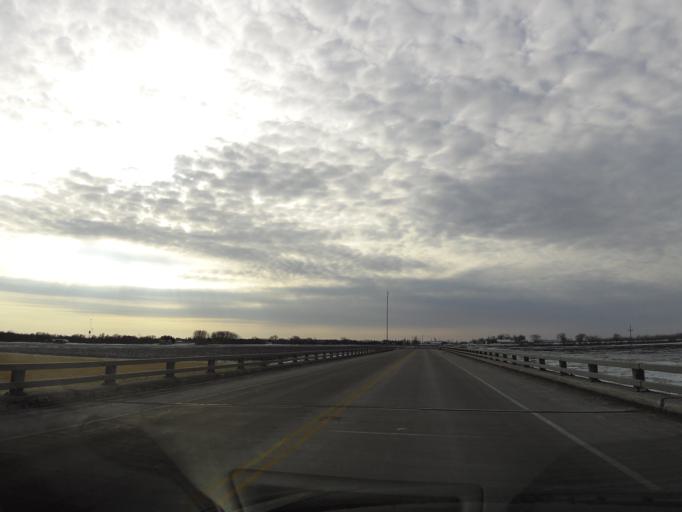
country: US
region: Minnesota
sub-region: Kittson County
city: Hallock
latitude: 48.5717
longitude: -97.1598
